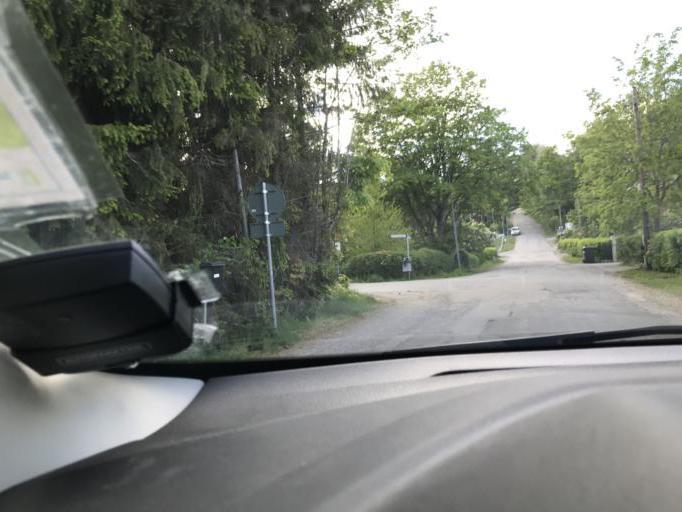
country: SE
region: Stockholm
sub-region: Botkyrka Kommun
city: Tumba
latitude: 59.1940
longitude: 17.8233
